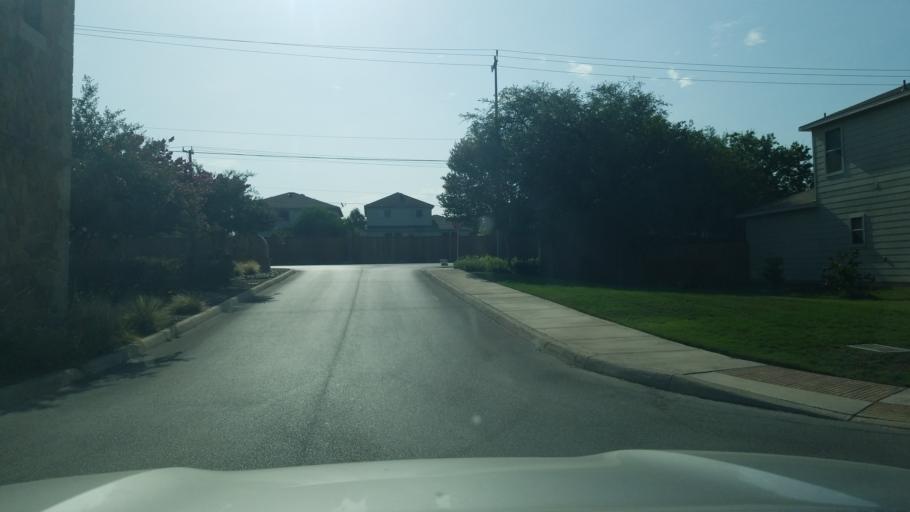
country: US
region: Texas
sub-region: Medina County
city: La Coste
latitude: 29.4344
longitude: -98.7484
